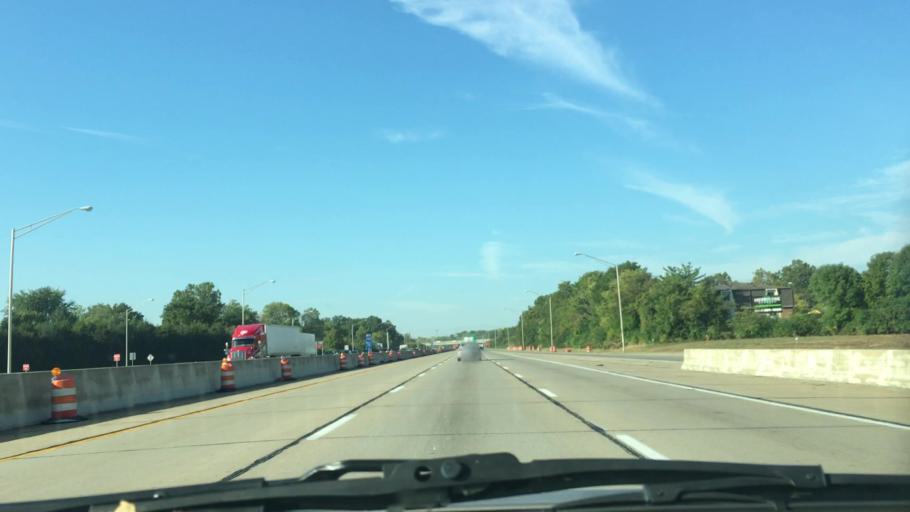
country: US
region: Indiana
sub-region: Marion County
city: Speedway
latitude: 39.7309
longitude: -86.2431
